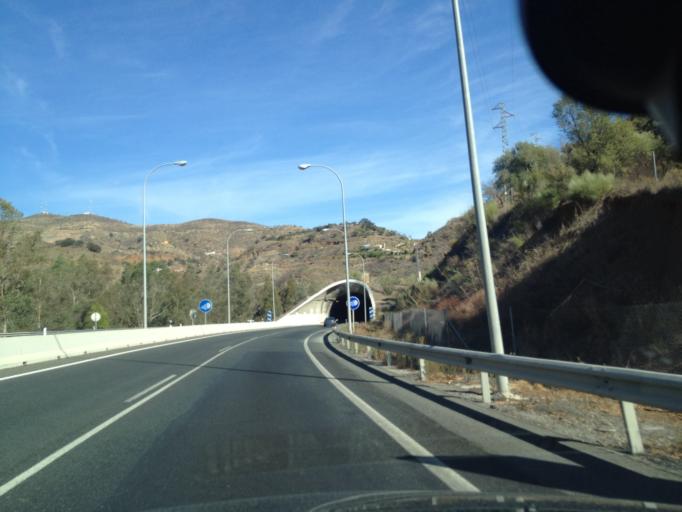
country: ES
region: Andalusia
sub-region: Provincia de Malaga
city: Casabermeja
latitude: 36.8698
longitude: -4.4361
